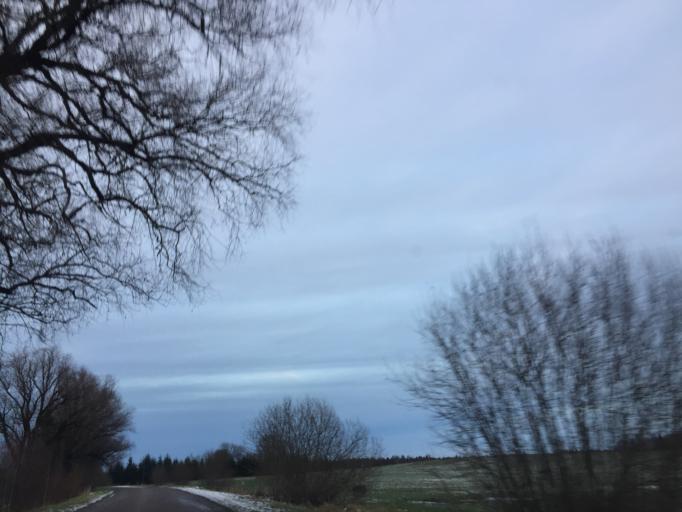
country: LV
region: Aloja
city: Aloja
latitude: 57.6188
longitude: 24.9260
